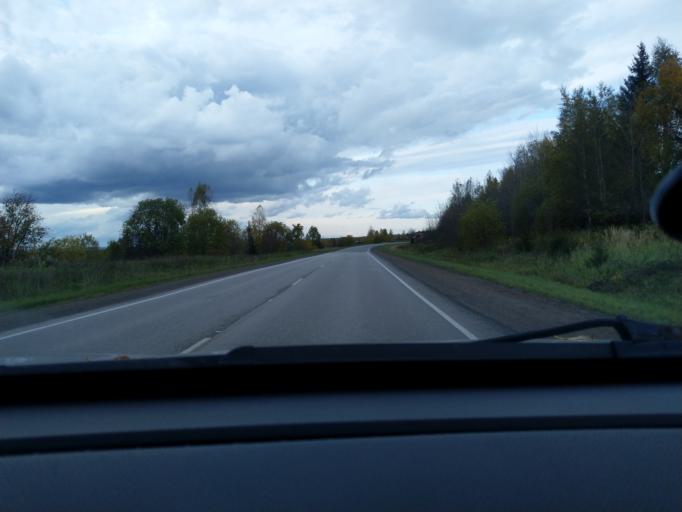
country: RU
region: Perm
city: Polazna
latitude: 58.3713
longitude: 56.4837
